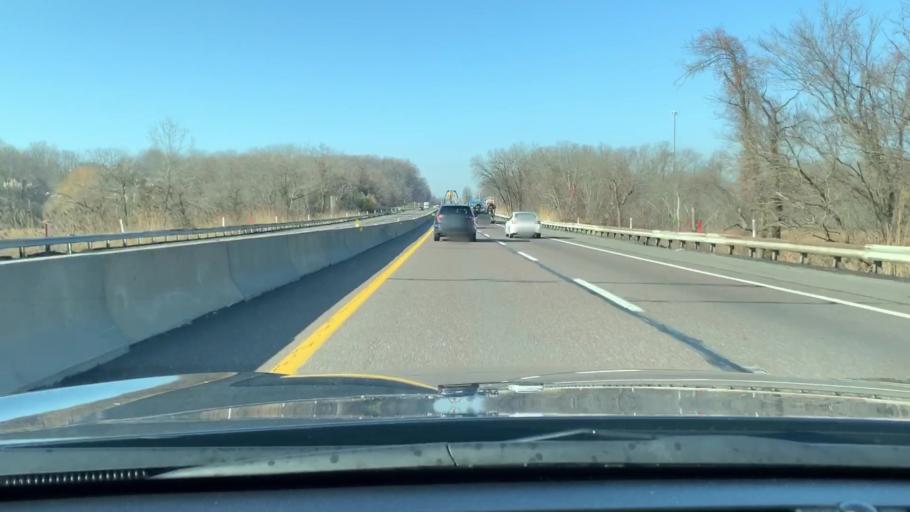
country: US
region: Pennsylvania
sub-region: Chester County
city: Elverson
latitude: 40.1184
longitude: -75.7698
